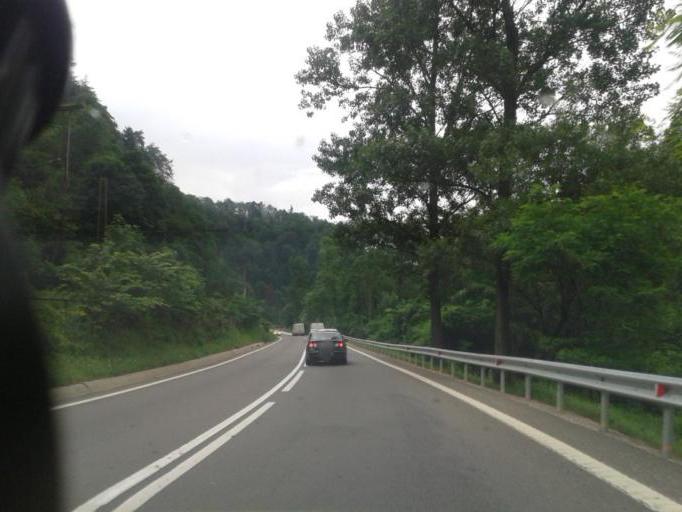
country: RO
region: Brasov
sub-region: Oras Predeal
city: Predeal
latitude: 45.5670
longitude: 25.6076
